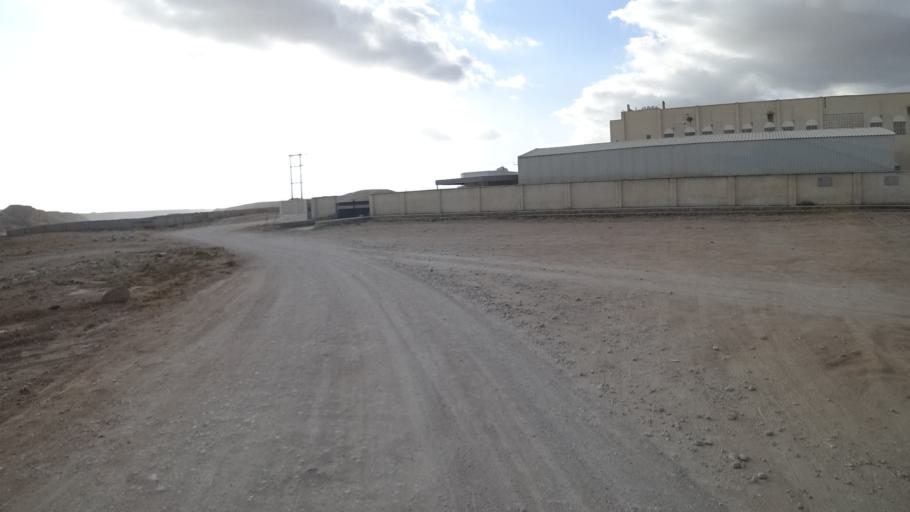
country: OM
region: Zufar
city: Salalah
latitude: 16.9602
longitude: 53.8684
